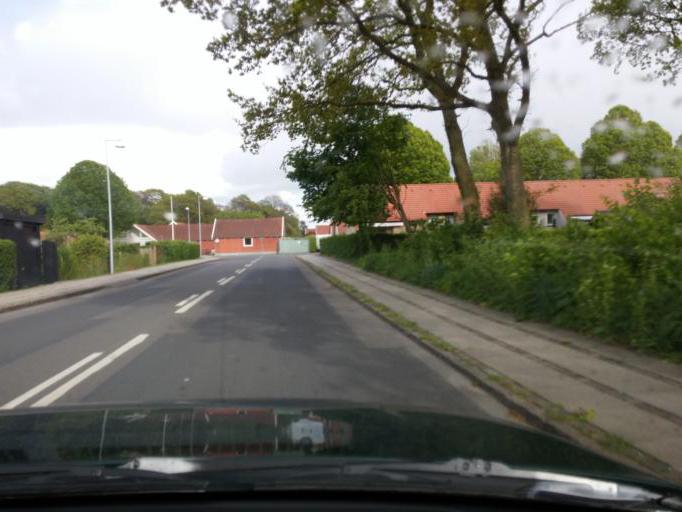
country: DK
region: South Denmark
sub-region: Odense Kommune
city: Stige
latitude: 55.4146
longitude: 10.4093
